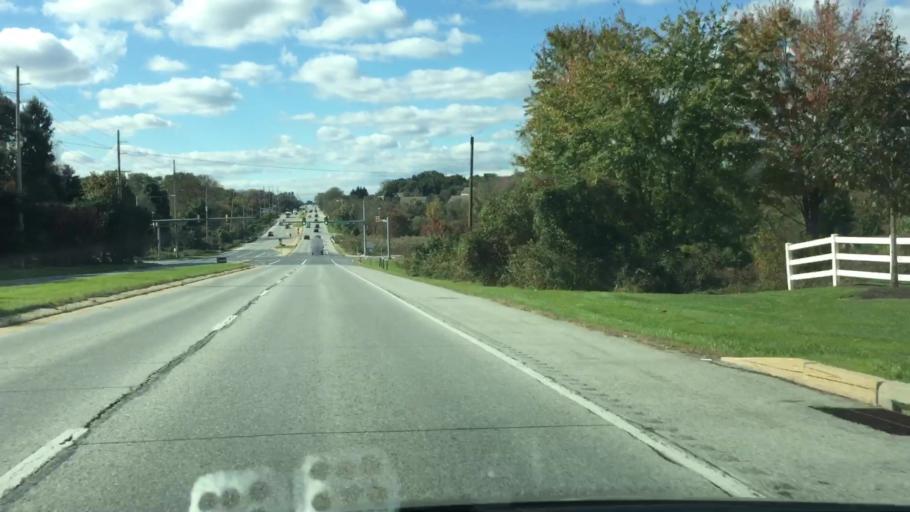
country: US
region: Pennsylvania
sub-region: Chester County
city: Malvern
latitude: 39.9654
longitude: -75.5050
